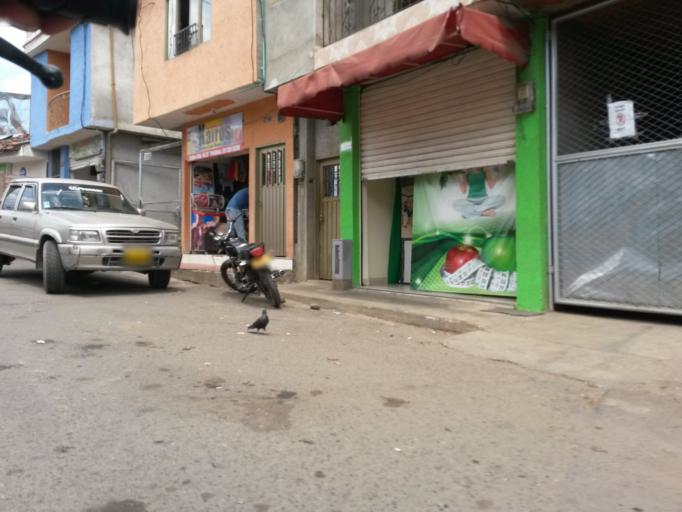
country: CO
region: Cauca
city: Santander de Quilichao
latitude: 3.0085
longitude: -76.4870
